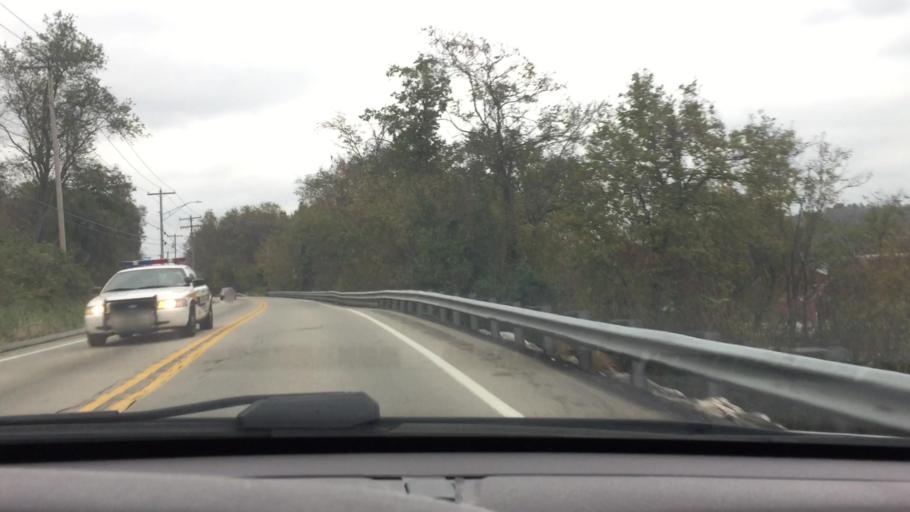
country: US
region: Pennsylvania
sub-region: Fayette County
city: Fairhope
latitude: 40.0882
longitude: -79.8460
